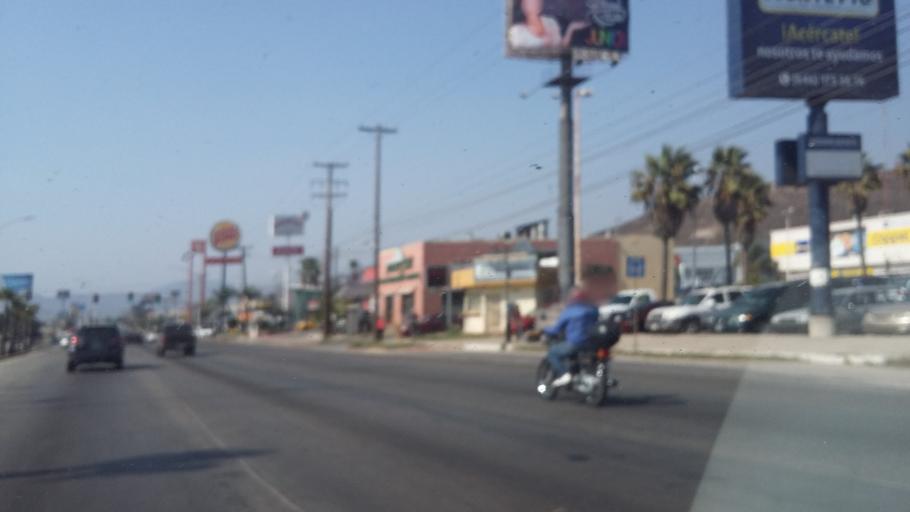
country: MX
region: Baja California
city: Ensenada
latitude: 31.8134
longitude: -116.5972
